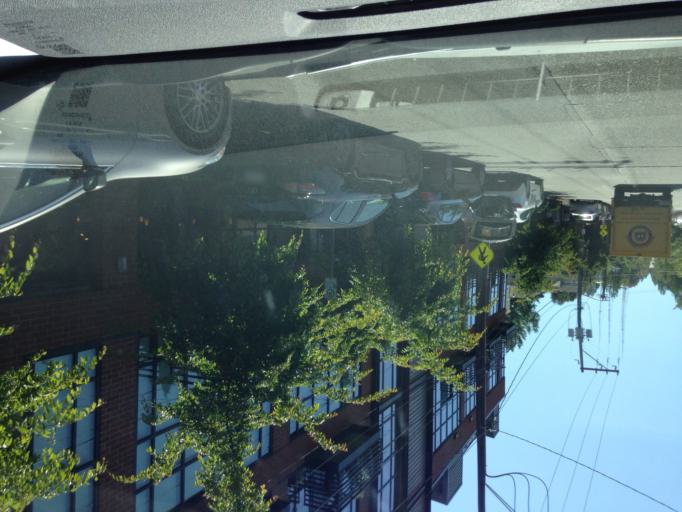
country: US
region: Washington
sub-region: King County
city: Seattle
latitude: 47.6249
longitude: -122.2941
